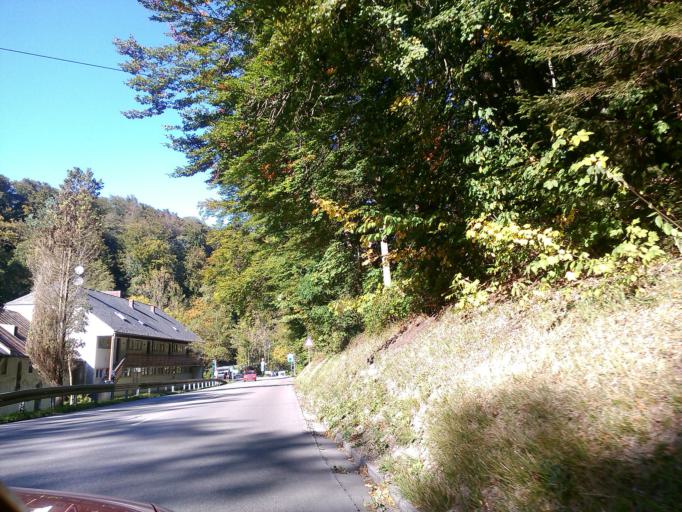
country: DE
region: Bavaria
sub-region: Upper Bavaria
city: Starnberg
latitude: 48.0342
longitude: 11.3588
